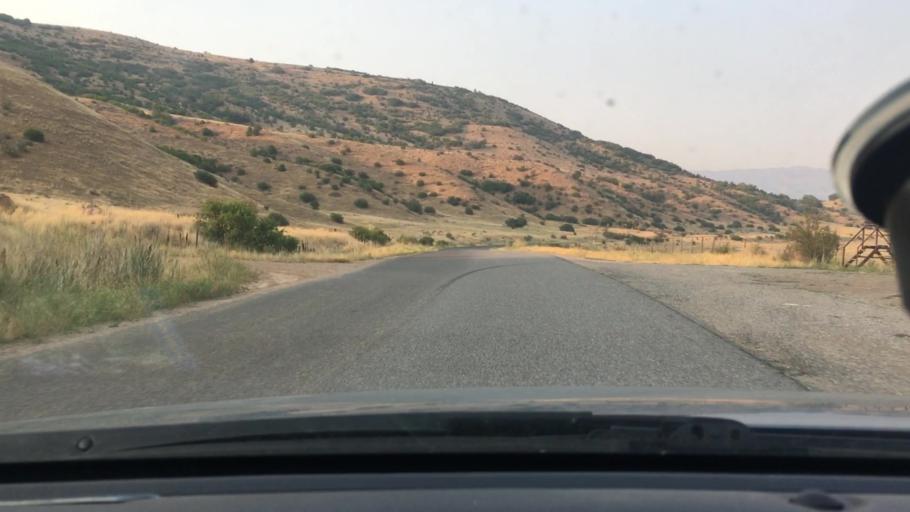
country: US
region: Utah
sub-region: Utah County
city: Mapleton
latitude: 40.0439
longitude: -111.4794
